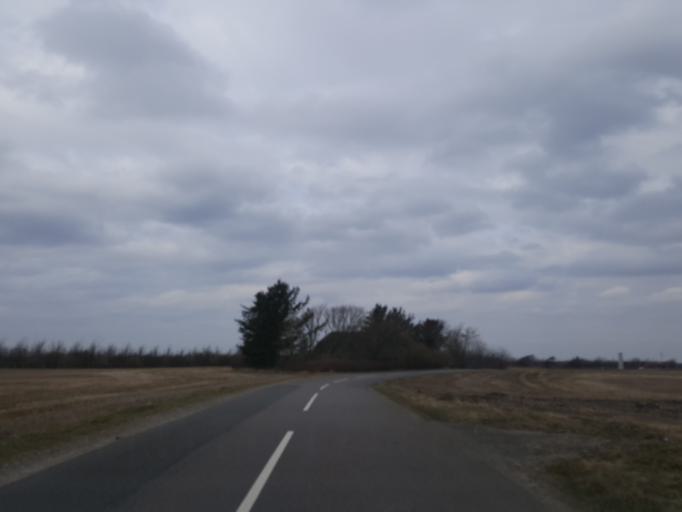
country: DK
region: Central Jutland
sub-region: Lemvig Kommune
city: Lemvig
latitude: 56.4169
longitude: 8.2333
